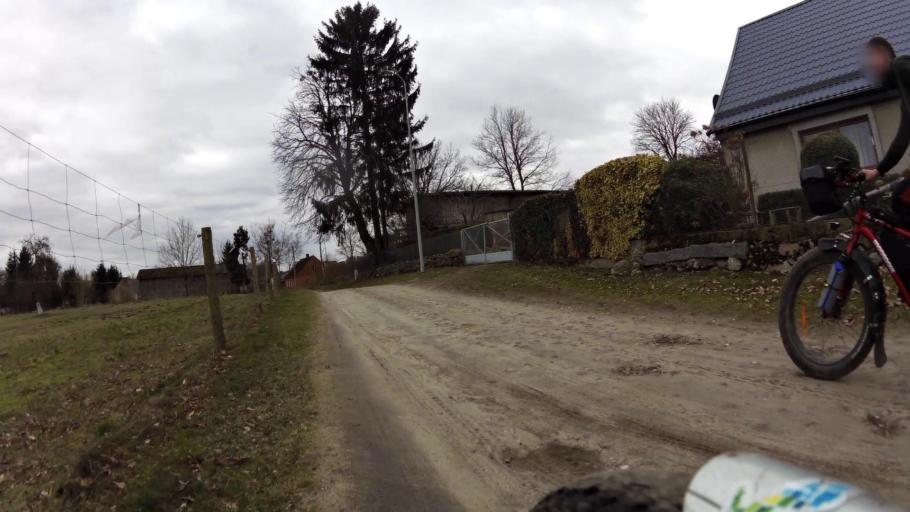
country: PL
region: Pomeranian Voivodeship
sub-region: Powiat bytowski
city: Trzebielino
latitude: 54.1079
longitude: 17.1300
